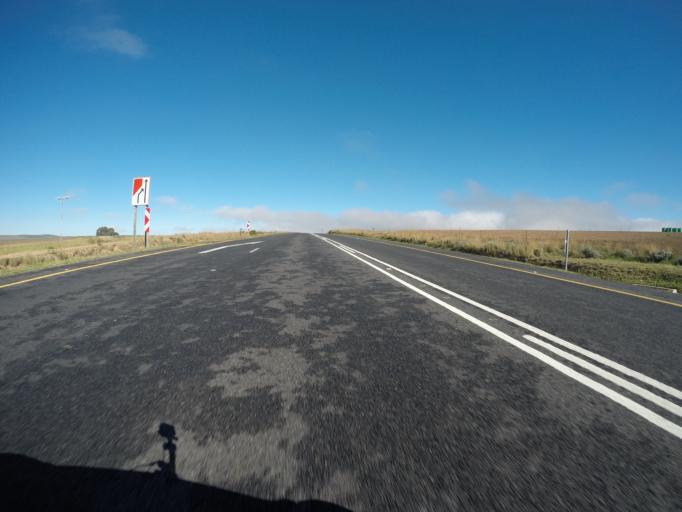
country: ZA
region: Western Cape
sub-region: Cape Winelands District Municipality
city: Ashton
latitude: -34.1362
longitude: 20.0267
